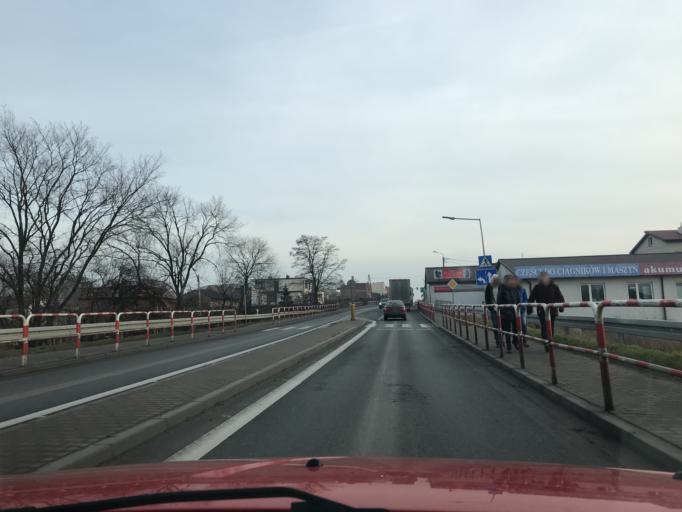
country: PL
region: Greater Poland Voivodeship
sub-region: Powiat ostrowski
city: Nowe Skalmierzyce
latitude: 51.7861
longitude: 18.0085
